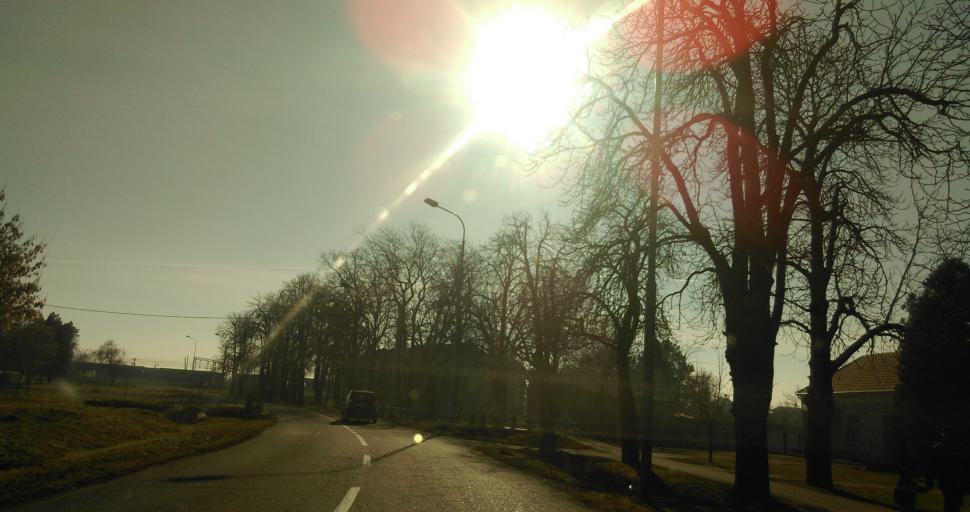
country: RS
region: Autonomna Pokrajina Vojvodina
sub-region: Sremski Okrug
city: Ruma
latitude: 44.9916
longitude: 19.8231
